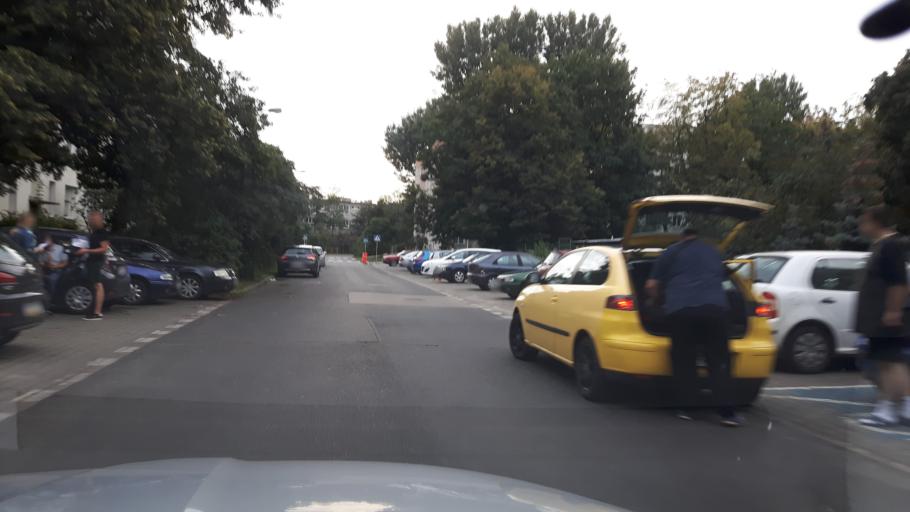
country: PL
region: Masovian Voivodeship
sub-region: Warszawa
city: Targowek
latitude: 52.2886
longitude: 21.0448
